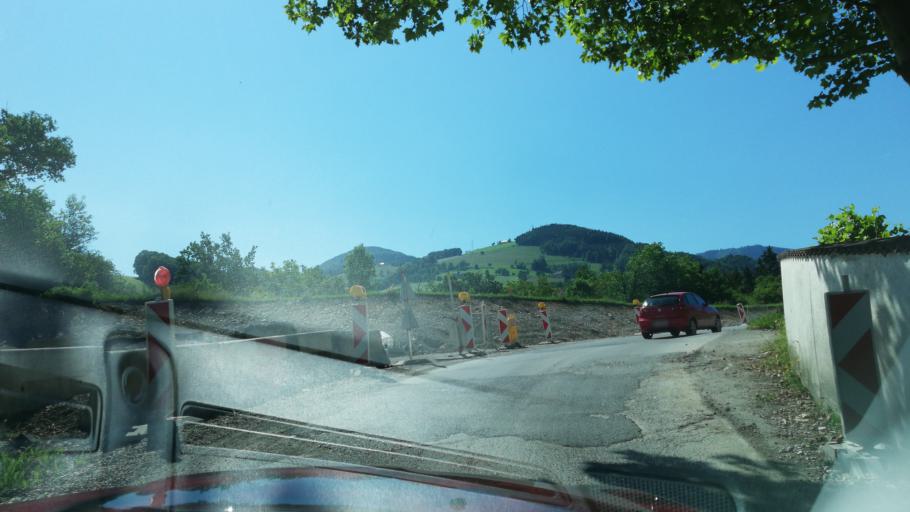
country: AT
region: Upper Austria
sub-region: Politischer Bezirk Kirchdorf an der Krems
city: Gruenburg
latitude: 47.9625
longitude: 14.2555
